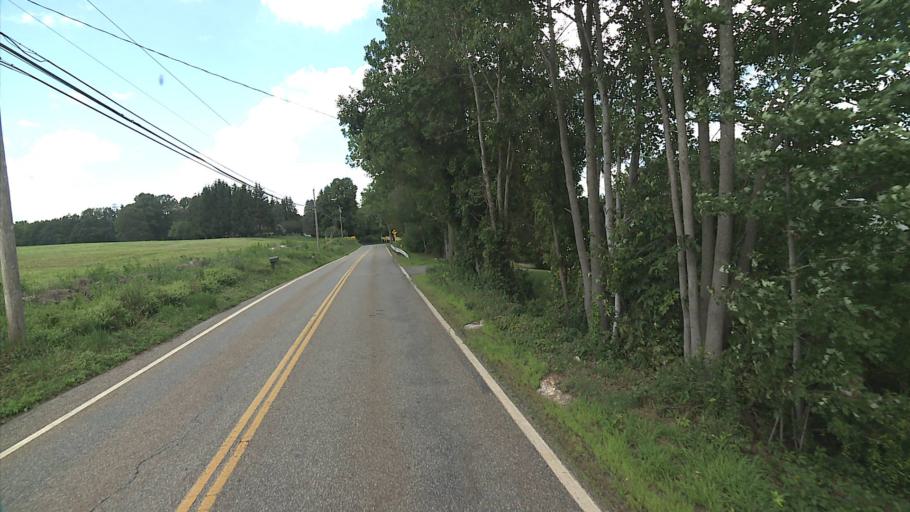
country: US
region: Connecticut
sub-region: Tolland County
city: Stafford
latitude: 41.9472
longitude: -72.1919
